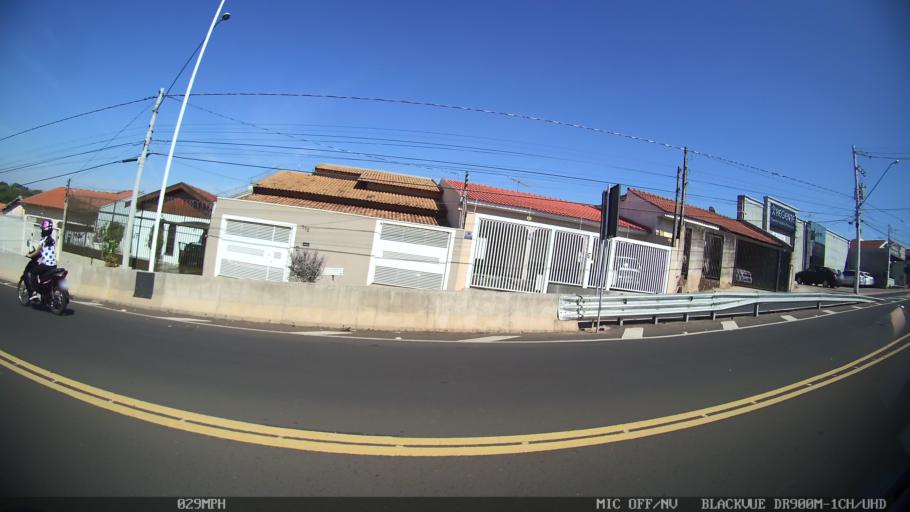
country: BR
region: Sao Paulo
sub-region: Sao Jose Do Rio Preto
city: Sao Jose do Rio Preto
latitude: -20.7876
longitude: -49.3902
